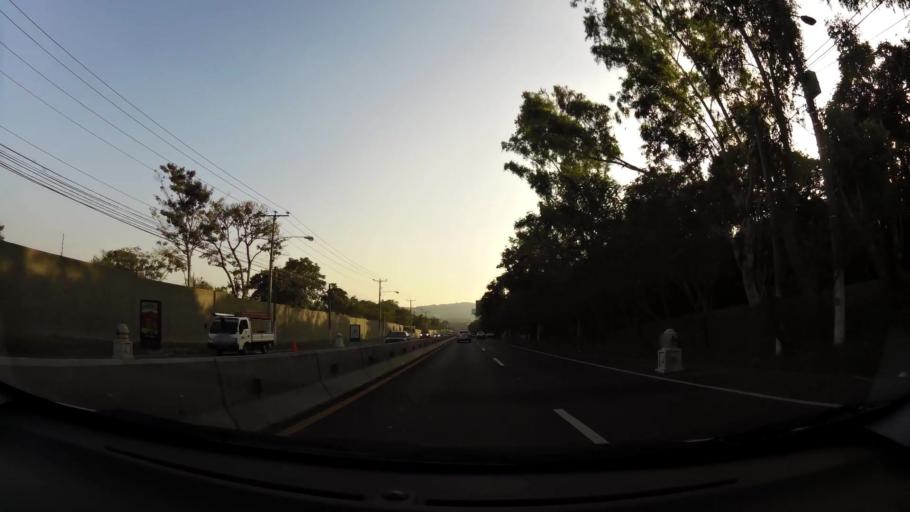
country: SV
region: La Libertad
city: Antiguo Cuscatlan
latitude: 13.6930
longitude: -89.2503
